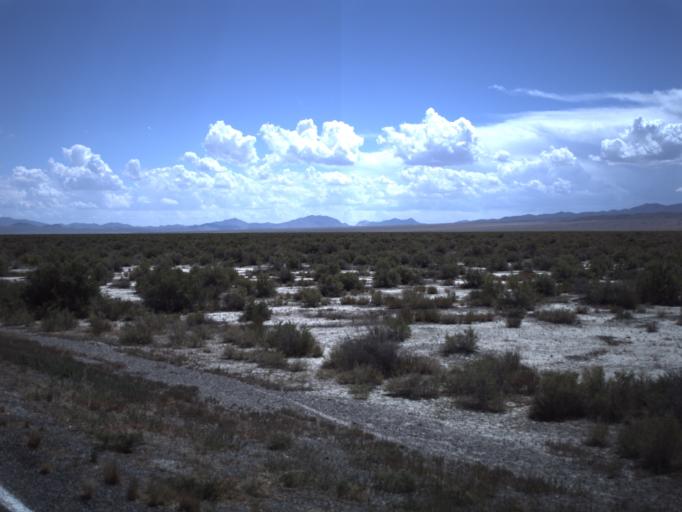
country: US
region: Nevada
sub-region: White Pine County
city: McGill
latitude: 39.0485
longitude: -113.9358
